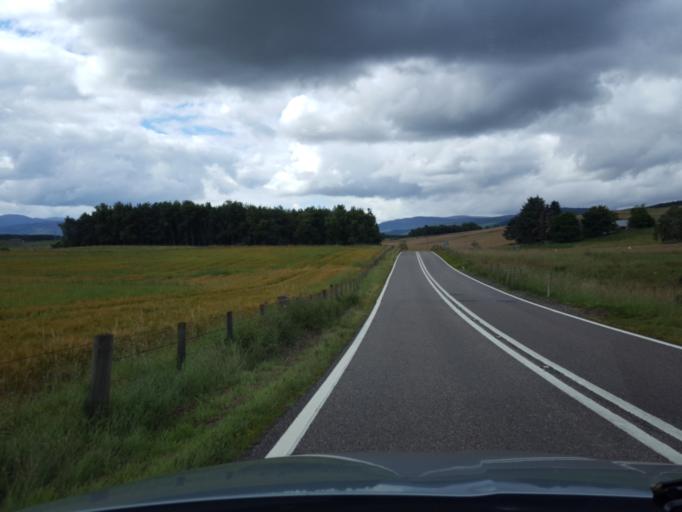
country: GB
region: Scotland
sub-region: Highland
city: Grantown on Spey
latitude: 57.2714
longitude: -3.7193
